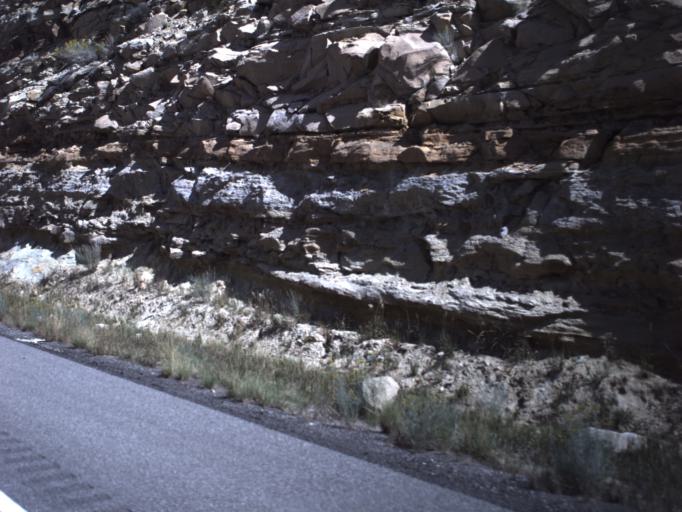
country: US
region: Utah
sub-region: Emery County
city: Ferron
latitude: 38.8565
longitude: -110.8695
